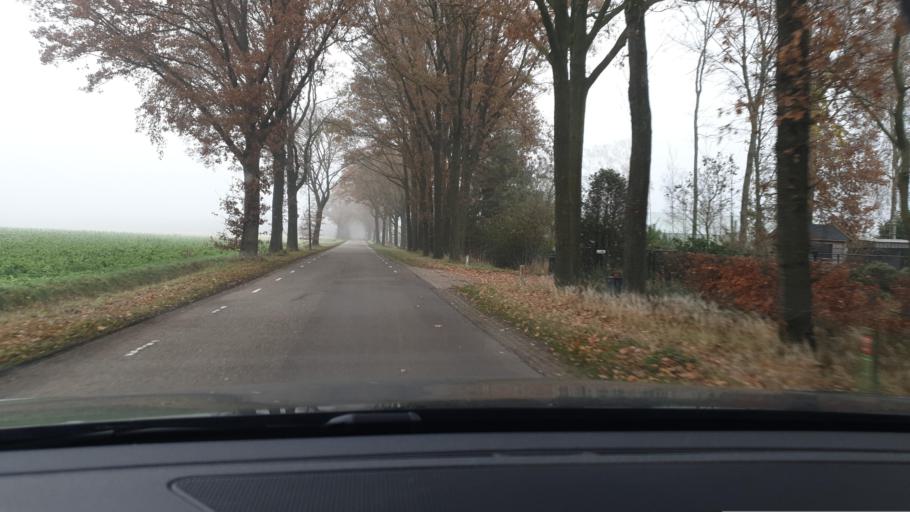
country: NL
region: North Brabant
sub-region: Gemeente Bladel en Netersel
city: Bladel
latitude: 51.3931
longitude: 5.1920
